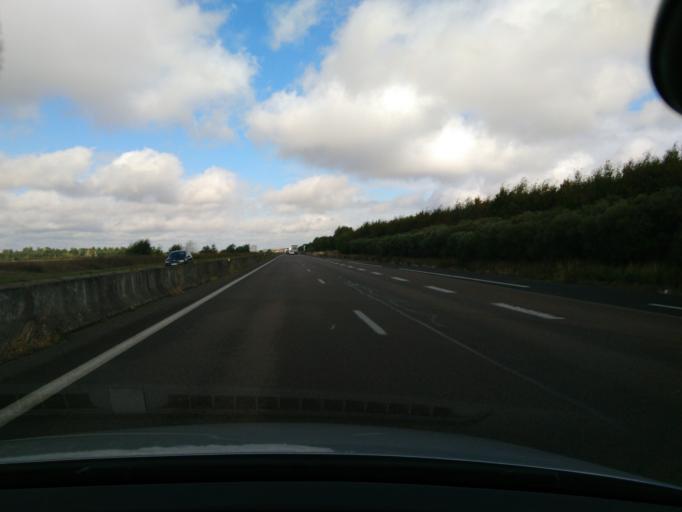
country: FR
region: Haute-Normandie
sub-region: Departement de l'Eure
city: Damville
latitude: 48.8720
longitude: 1.1760
